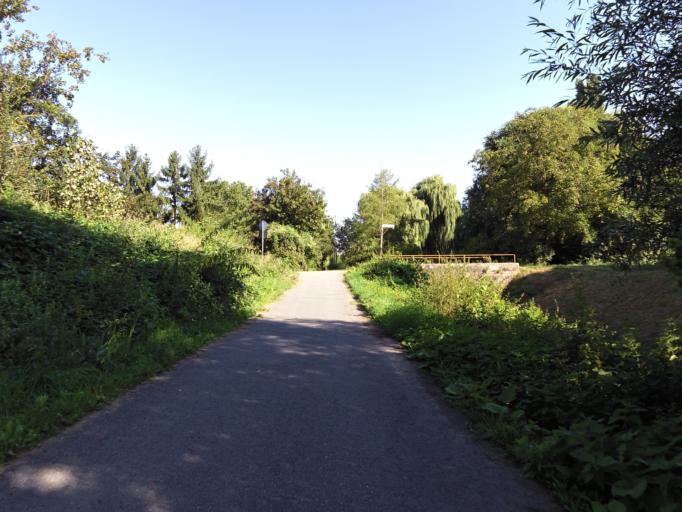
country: DE
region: Hesse
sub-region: Regierungsbezirk Darmstadt
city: Stockstadt am Rhein
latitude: 49.8044
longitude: 8.4532
